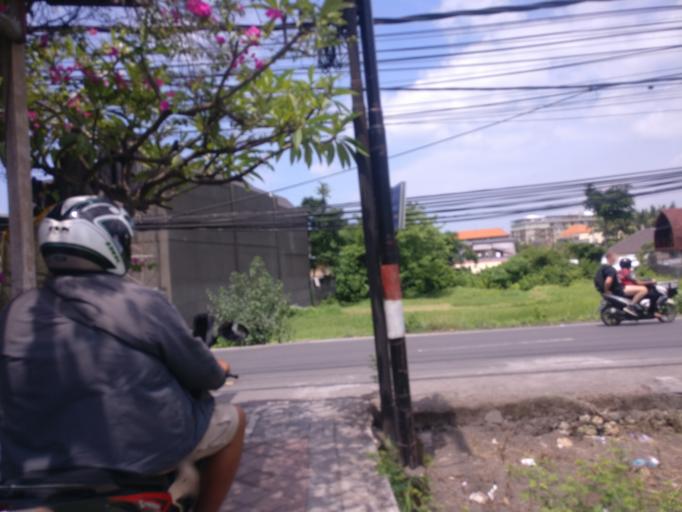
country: ID
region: Bali
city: Kuta
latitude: -8.6780
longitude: 115.1607
